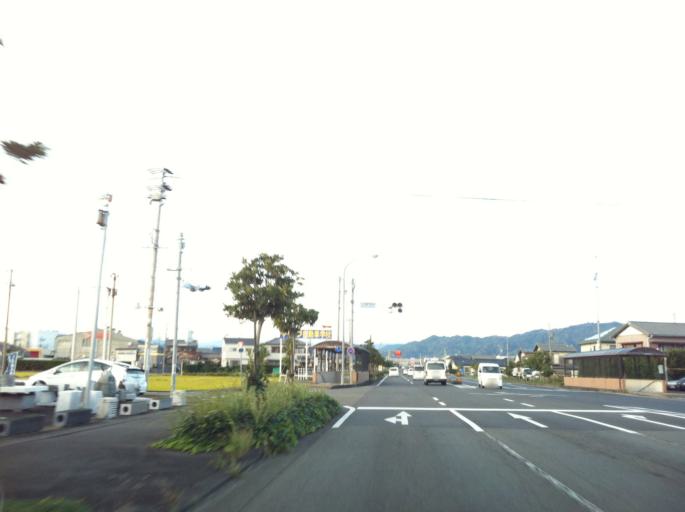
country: JP
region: Shizuoka
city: Yaizu
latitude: 34.8467
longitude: 138.2997
